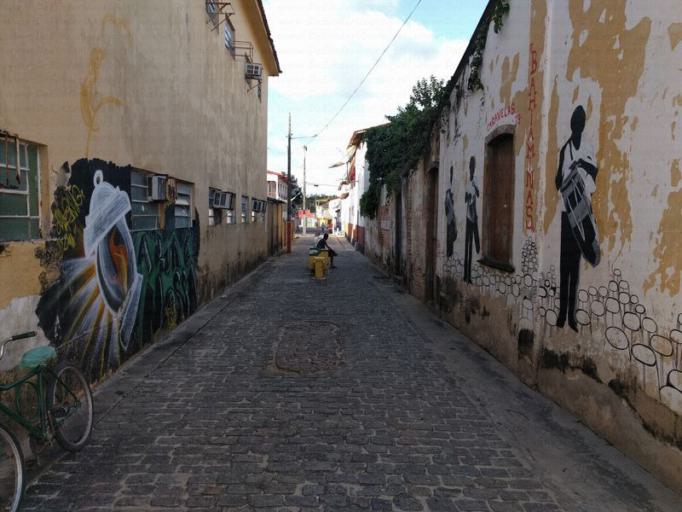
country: BR
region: Bahia
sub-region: Nova Vicosa
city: Nova Vicosa
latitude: -17.7340
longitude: -39.2656
